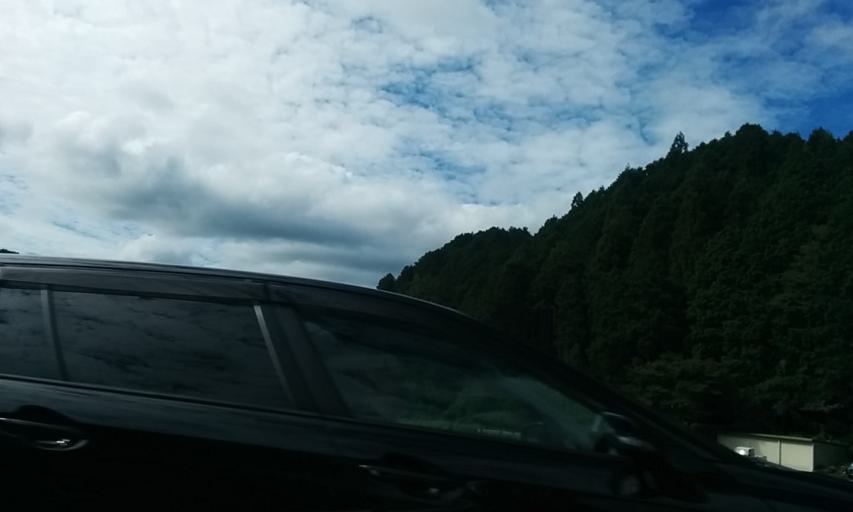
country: JP
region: Gifu
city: Minokamo
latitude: 35.5787
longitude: 137.0890
